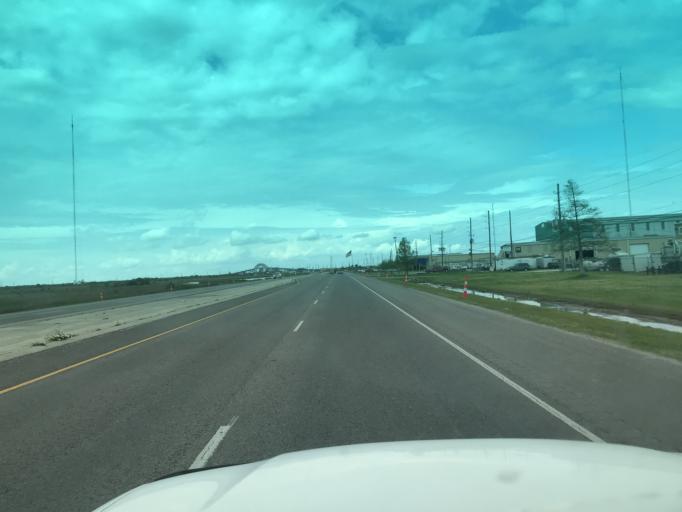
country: US
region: Louisiana
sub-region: Saint Bernard Parish
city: Chalmette
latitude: 29.9722
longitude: -89.9490
